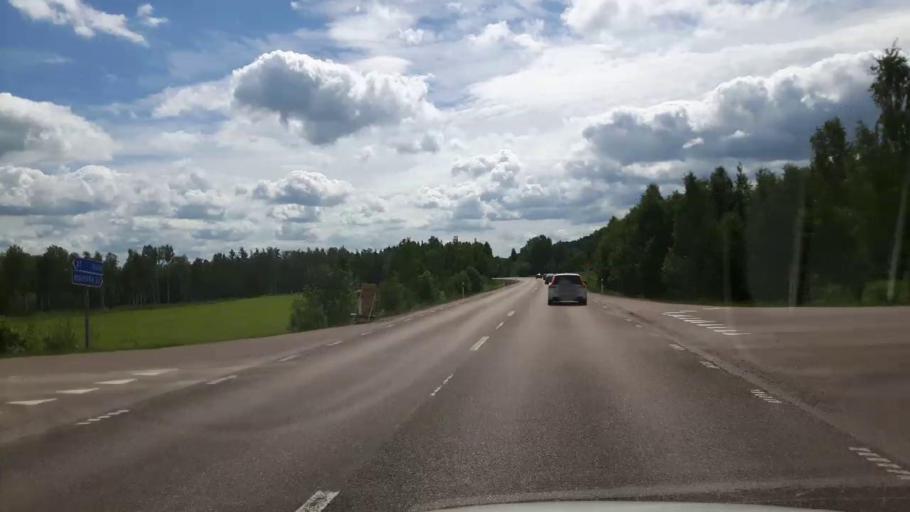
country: SE
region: Dalarna
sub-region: Saters Kommun
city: Saeter
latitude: 60.4501
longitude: 15.8073
